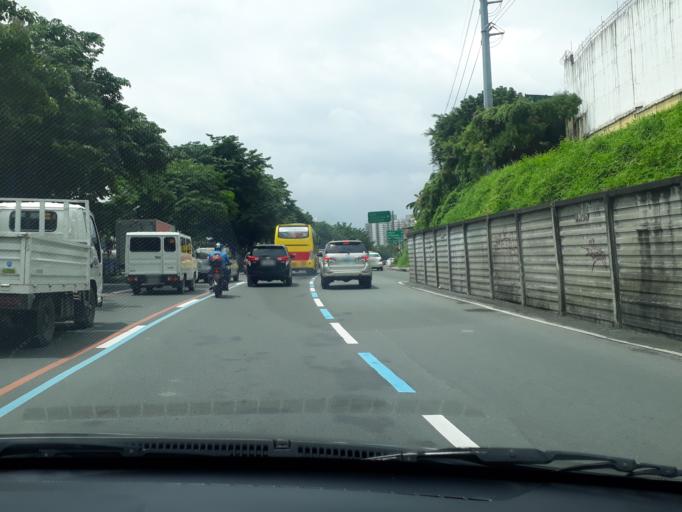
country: PH
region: Calabarzon
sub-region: Province of Rizal
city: Pateros
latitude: 14.5388
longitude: 121.0572
